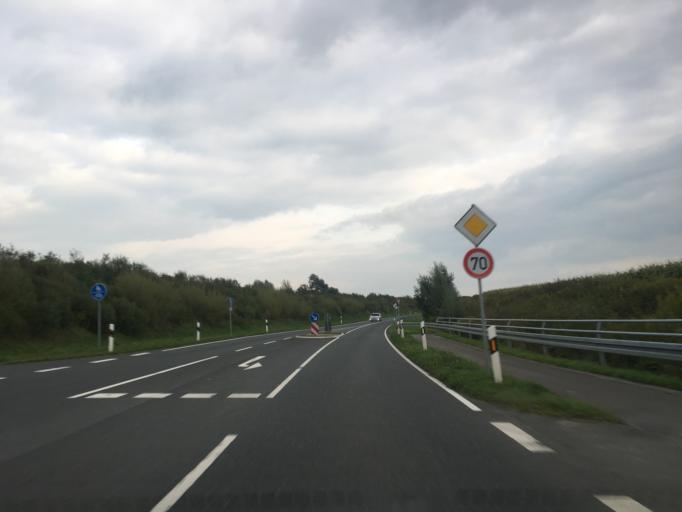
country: DE
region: North Rhine-Westphalia
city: Olfen
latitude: 51.7039
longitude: 7.3625
